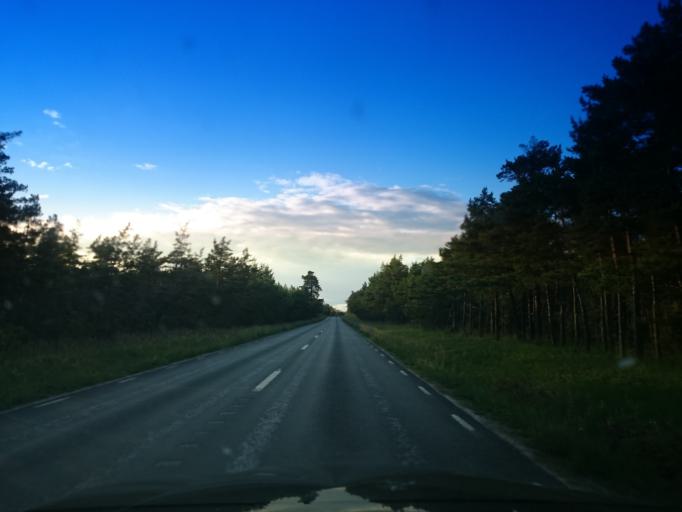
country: SE
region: Gotland
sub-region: Gotland
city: Hemse
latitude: 57.3335
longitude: 18.3793
